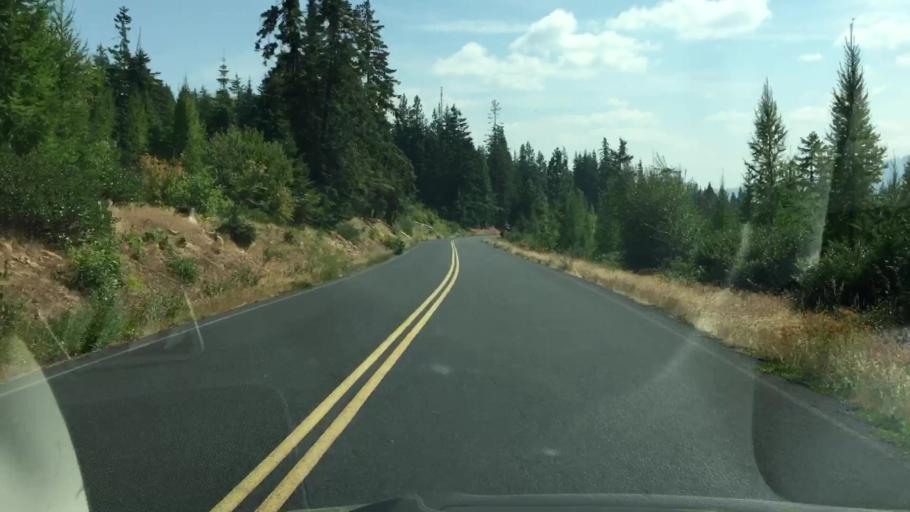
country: US
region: Washington
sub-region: Klickitat County
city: White Salmon
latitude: 46.0335
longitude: -121.5445
